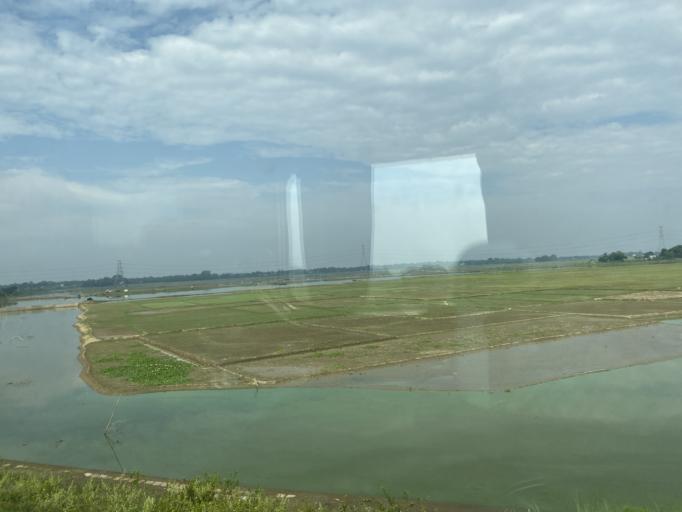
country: IN
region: Tripura
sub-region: West Tripura
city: Agartala
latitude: 23.8802
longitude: 91.2037
